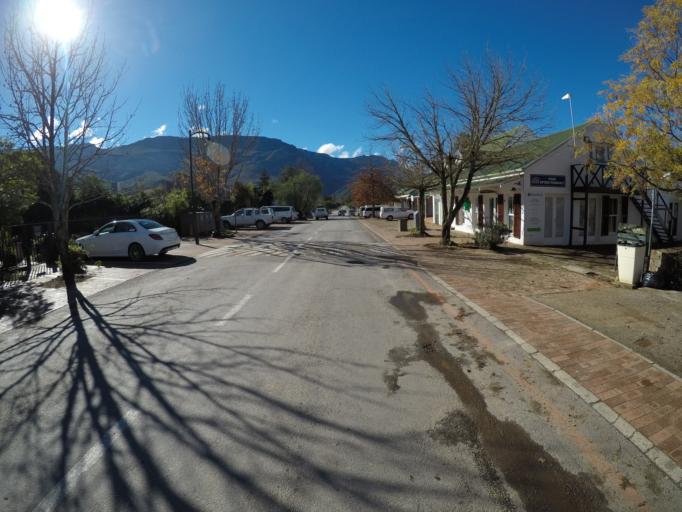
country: ZA
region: Western Cape
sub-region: Overberg District Municipality
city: Caledon
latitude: -34.0504
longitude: 19.6077
